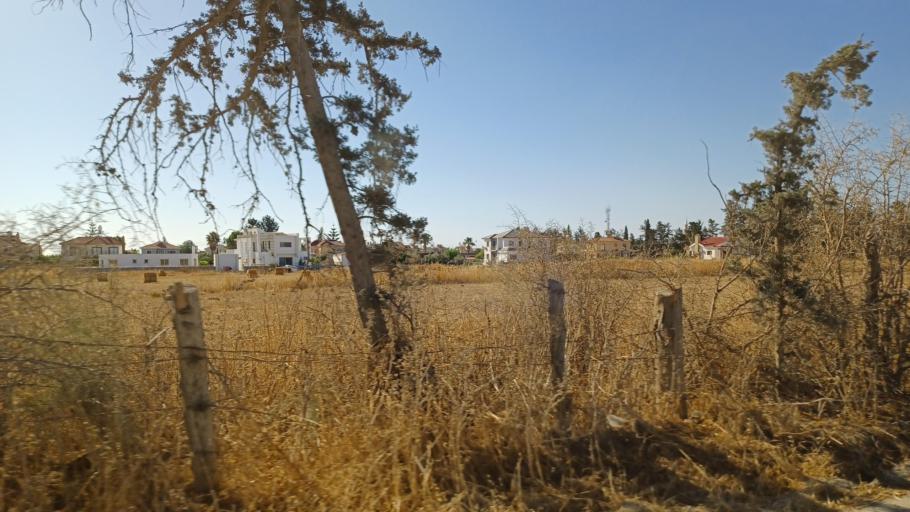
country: CY
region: Larnaka
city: Pergamos
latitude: 35.0441
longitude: 33.7038
